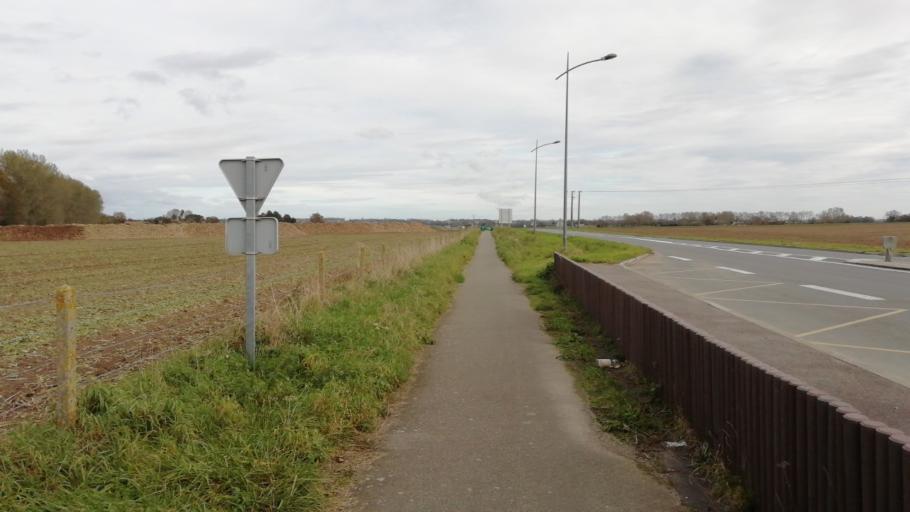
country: FR
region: Haute-Normandie
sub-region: Departement de la Seine-Maritime
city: Cauville-sur-Mer
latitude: 49.5947
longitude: 0.1342
